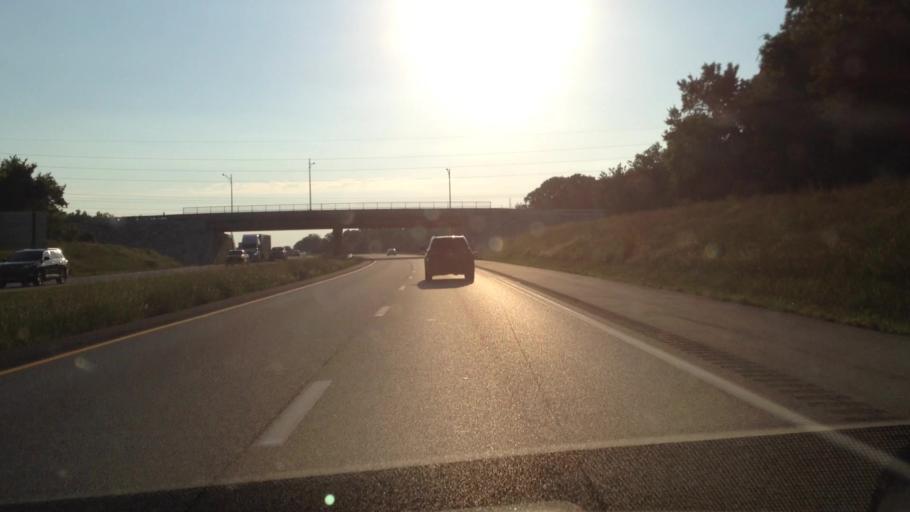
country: US
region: Missouri
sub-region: Jasper County
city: Joplin
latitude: 37.0458
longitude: -94.4946
